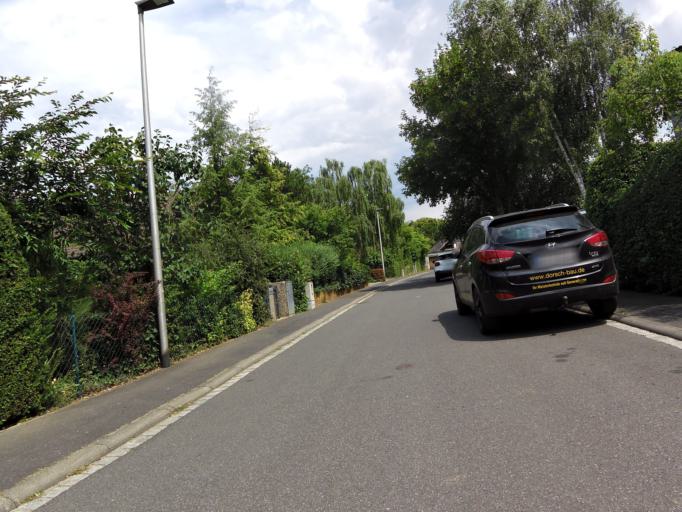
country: DE
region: Bavaria
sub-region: Regierungsbezirk Unterfranken
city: Eibelstadt
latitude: 49.7188
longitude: 9.9646
